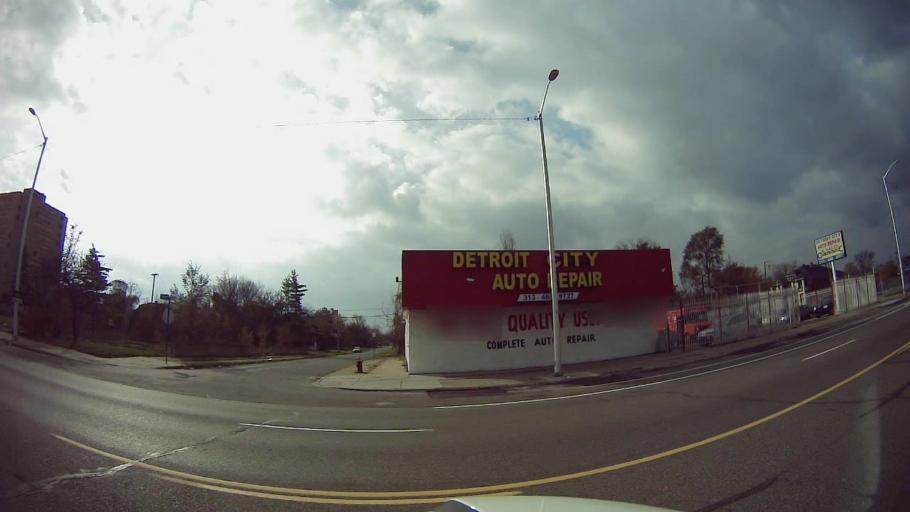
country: US
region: Michigan
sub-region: Wayne County
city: Highland Park
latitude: 42.3790
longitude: -83.1237
